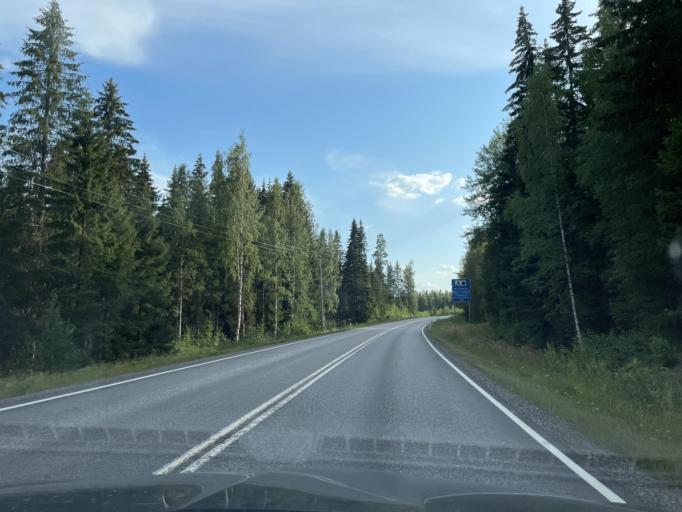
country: FI
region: Paijanne Tavastia
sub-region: Lahti
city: Auttoinen
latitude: 61.3135
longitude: 25.1270
